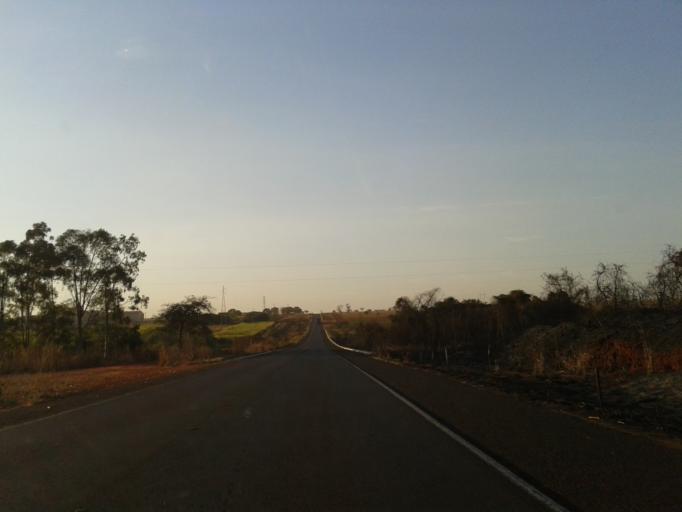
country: BR
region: Minas Gerais
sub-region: Santa Vitoria
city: Santa Vitoria
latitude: -19.0621
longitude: -50.3846
